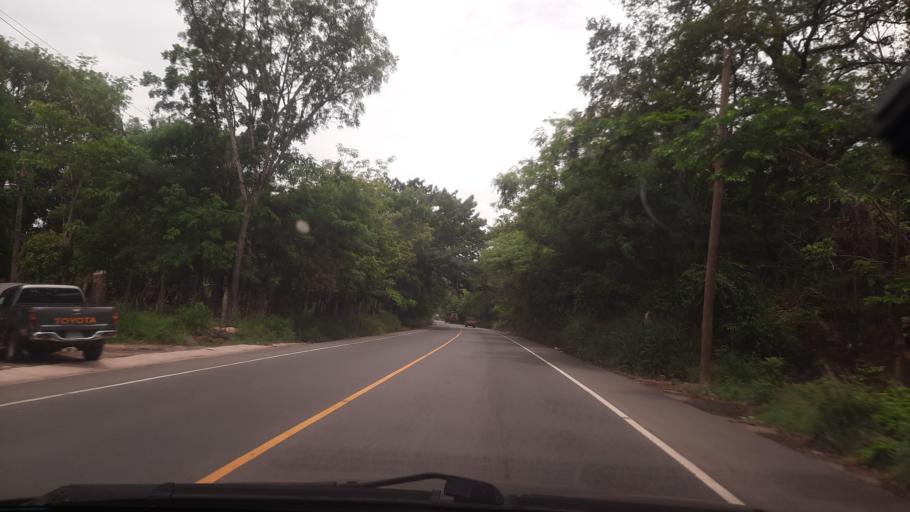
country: GT
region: Zacapa
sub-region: Municipio de Zacapa
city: Gualan
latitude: 15.1845
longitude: -89.2885
